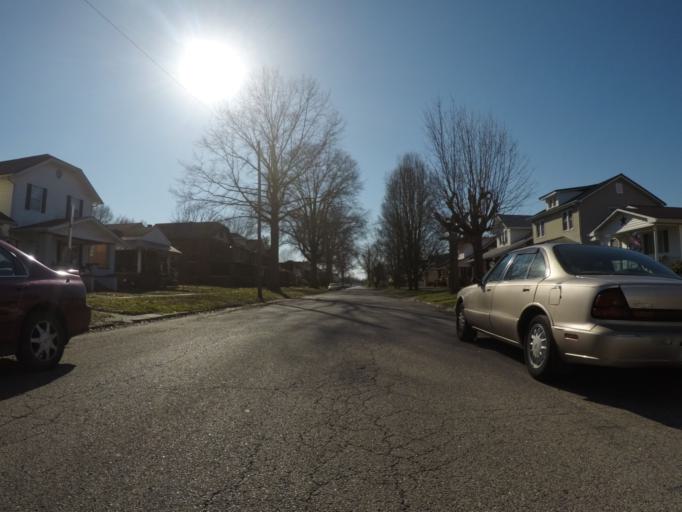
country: US
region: West Virginia
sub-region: Cabell County
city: Huntington
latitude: 38.4108
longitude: -82.4884
